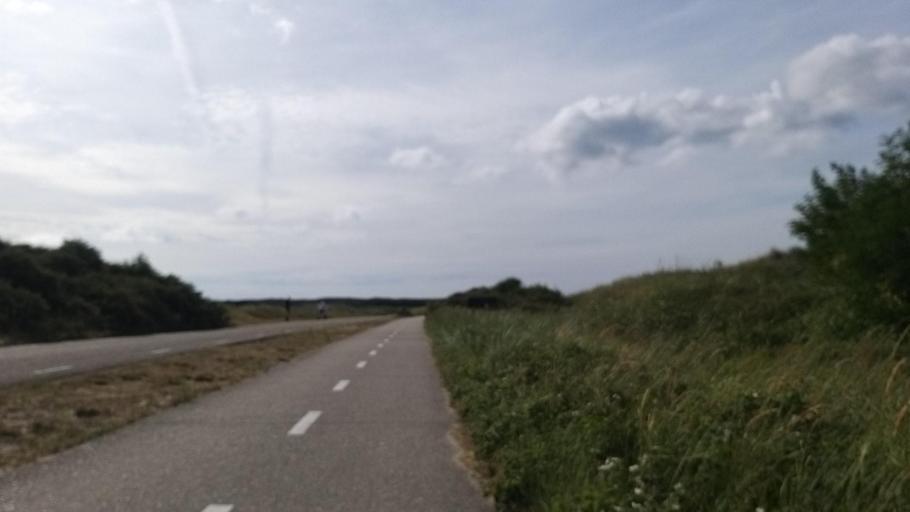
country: NL
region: North Holland
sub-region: Gemeente Texel
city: Den Burg
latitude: 53.1586
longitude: 4.8300
